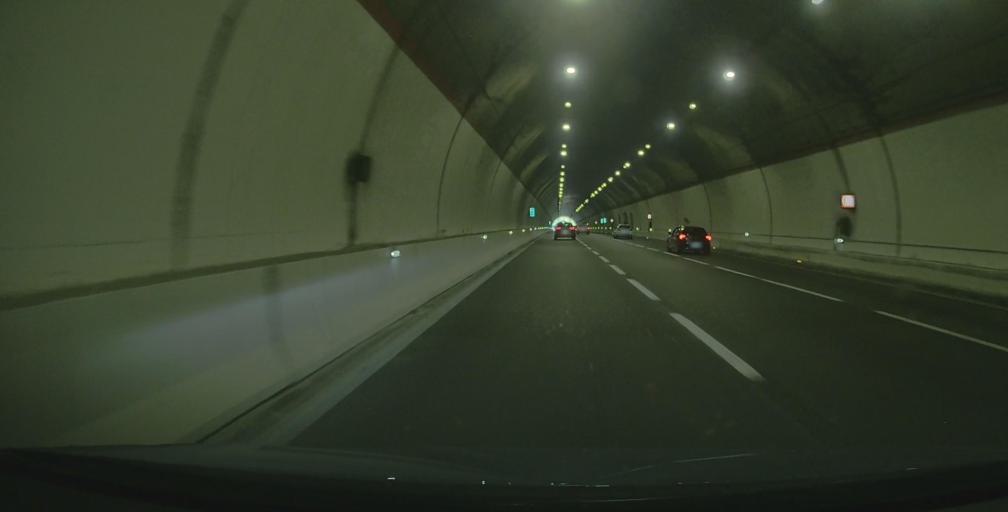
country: IT
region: Campania
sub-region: Provincia di Salerno
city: Pezzano-Filetta
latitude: 40.6730
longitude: 14.8578
